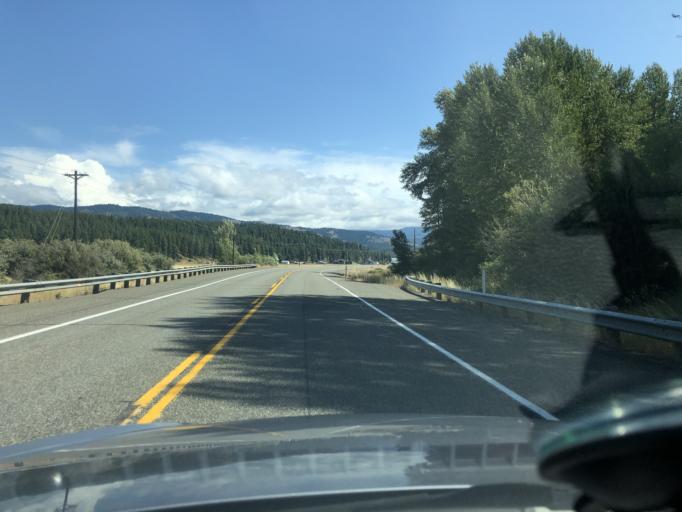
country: US
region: Washington
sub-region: Kittitas County
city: Cle Elum
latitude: 47.1922
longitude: -120.8102
